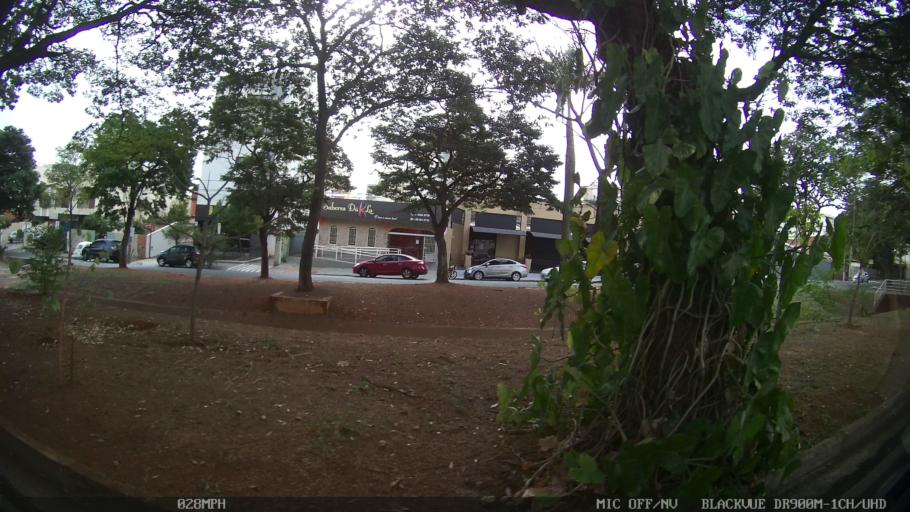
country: BR
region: Sao Paulo
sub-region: Sao Jose Do Rio Preto
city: Sao Jose do Rio Preto
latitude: -20.8335
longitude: -49.3835
